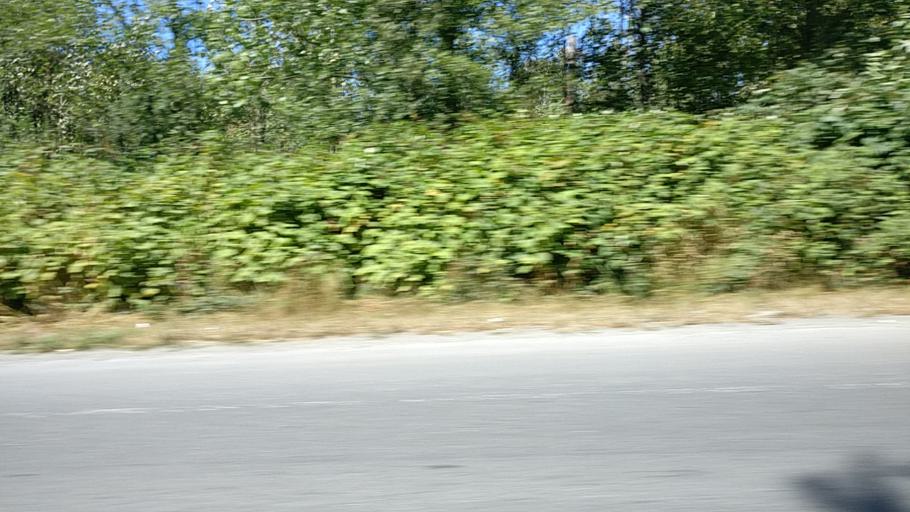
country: CA
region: British Columbia
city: Aldergrove
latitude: 49.0171
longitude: -122.4453
